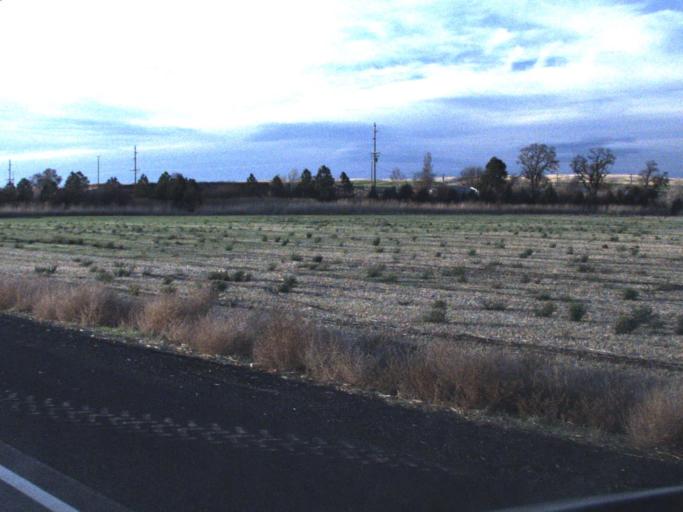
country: US
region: Washington
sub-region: Walla Walla County
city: Garrett
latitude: 46.0415
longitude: -118.6810
